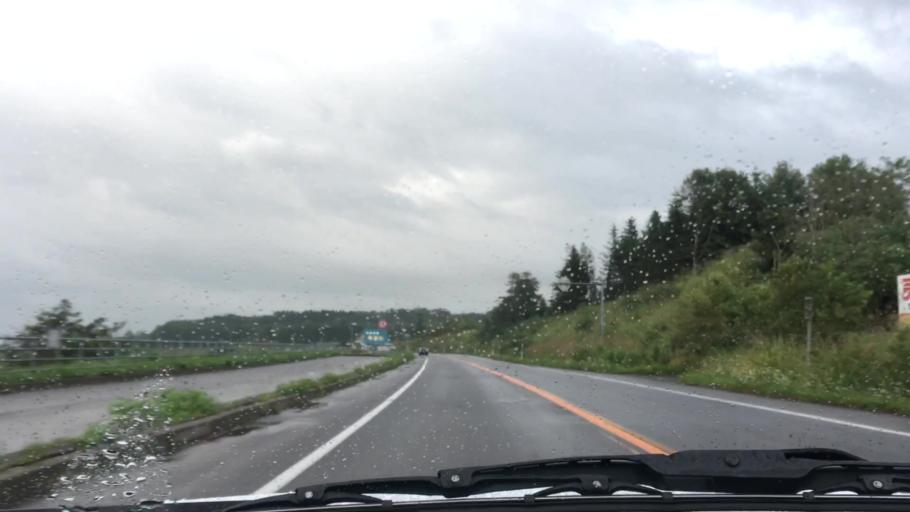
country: JP
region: Hokkaido
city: Nanae
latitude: 42.1806
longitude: 140.4407
